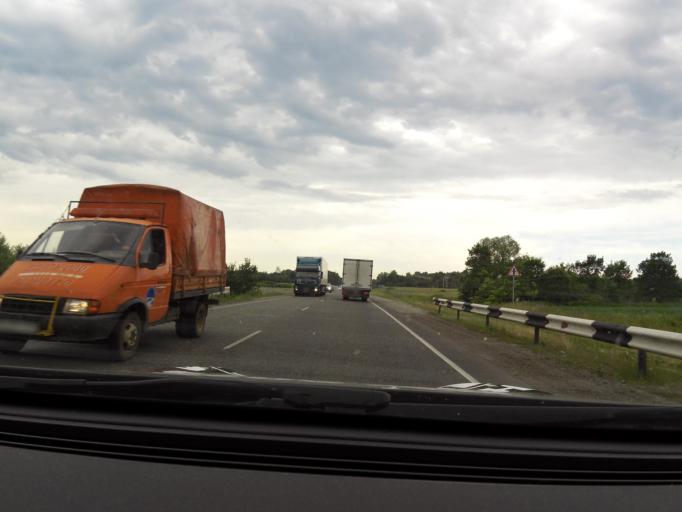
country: RU
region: Bashkortostan
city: Kudeyevskiy
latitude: 54.8143
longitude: 56.6870
